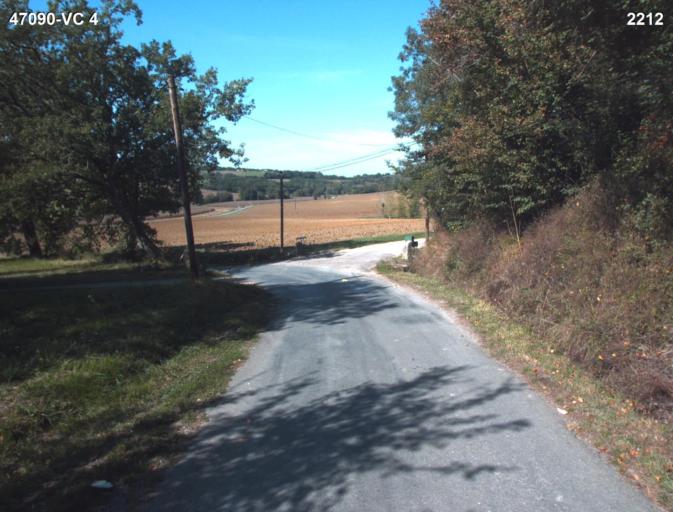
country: FR
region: Aquitaine
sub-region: Departement du Lot-et-Garonne
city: Nerac
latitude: 44.1753
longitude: 0.3664
